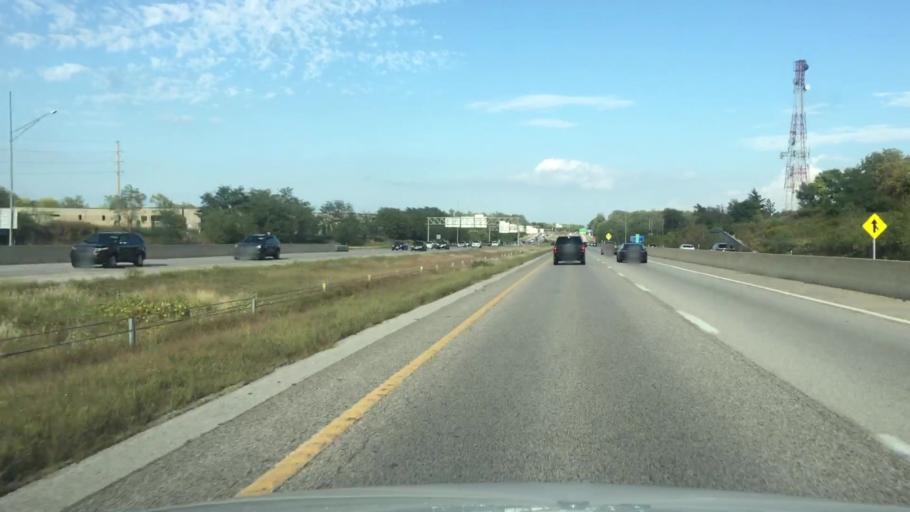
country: US
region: Missouri
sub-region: Jackson County
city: Lees Summit
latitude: 38.9368
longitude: -94.4007
